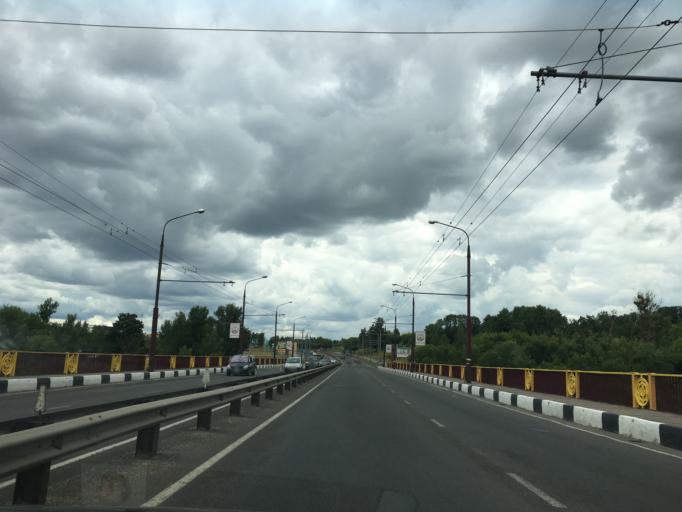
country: BY
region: Grodnenskaya
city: Hrodna
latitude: 53.6611
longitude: 23.8596
